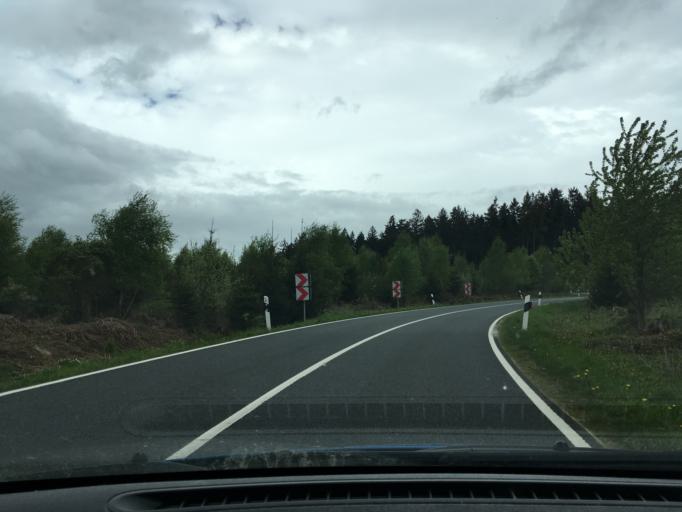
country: DE
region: Lower Saxony
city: Derental
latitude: 51.7563
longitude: 9.4961
